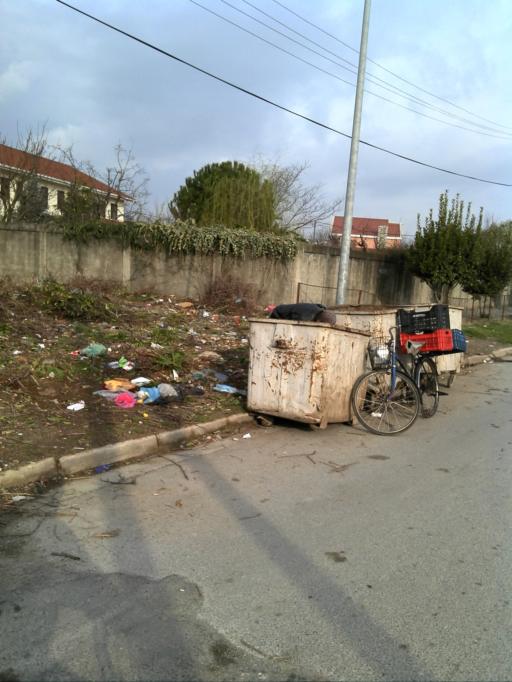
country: AL
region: Shkoder
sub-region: Rrethi i Shkodres
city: Shkoder
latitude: 42.0571
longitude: 19.5156
